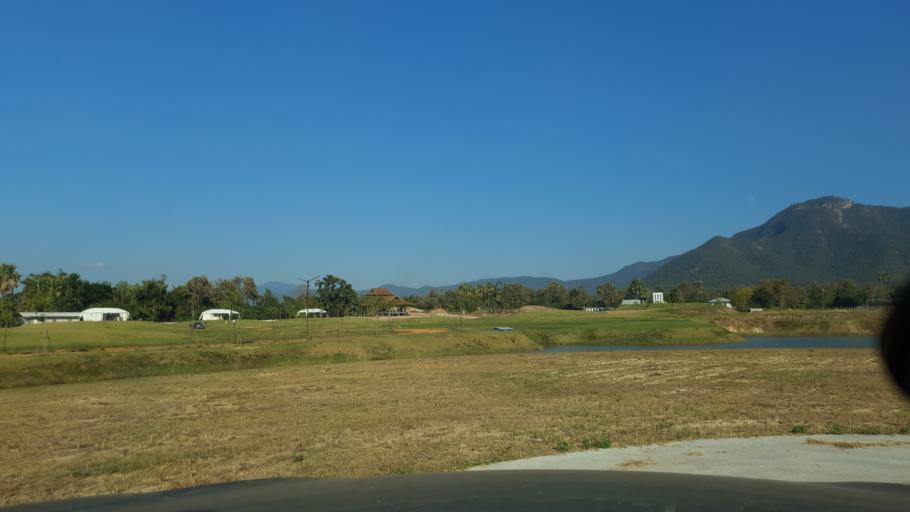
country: TH
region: Chiang Mai
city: Mae On
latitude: 18.7246
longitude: 99.2130
